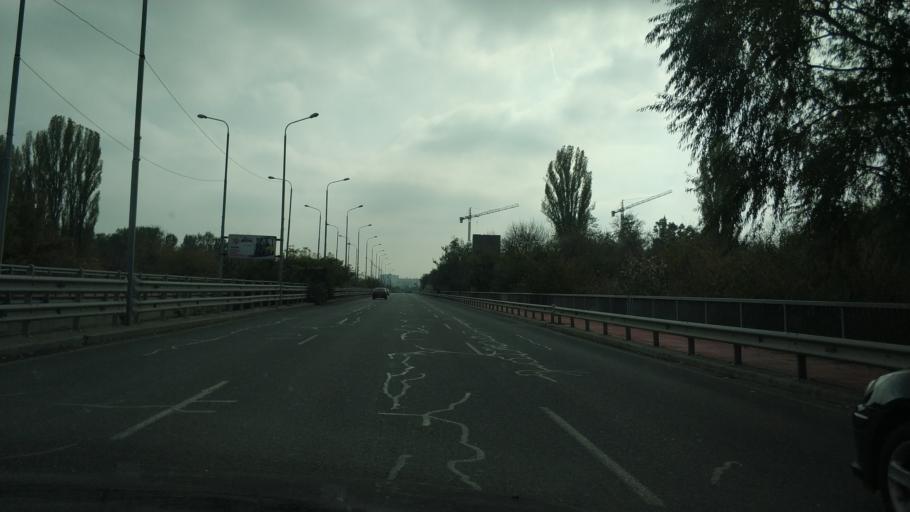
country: BG
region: Plovdiv
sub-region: Obshtina Plovdiv
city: Plovdiv
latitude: 42.1569
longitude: 24.7653
